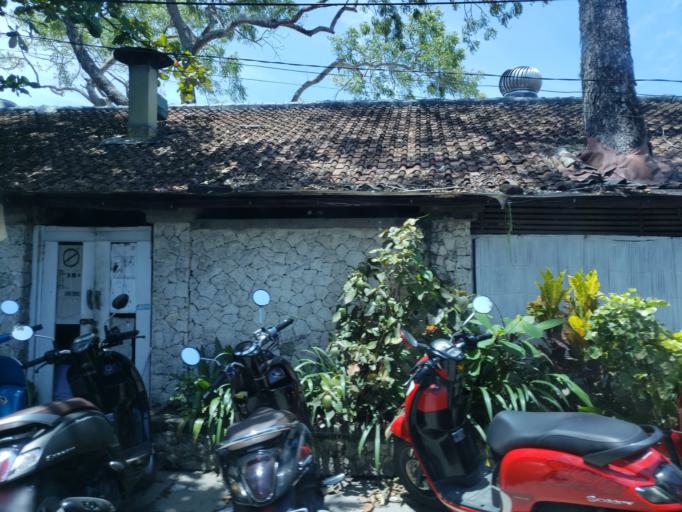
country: ID
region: Bali
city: Jimbaran
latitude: -8.7818
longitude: 115.1632
